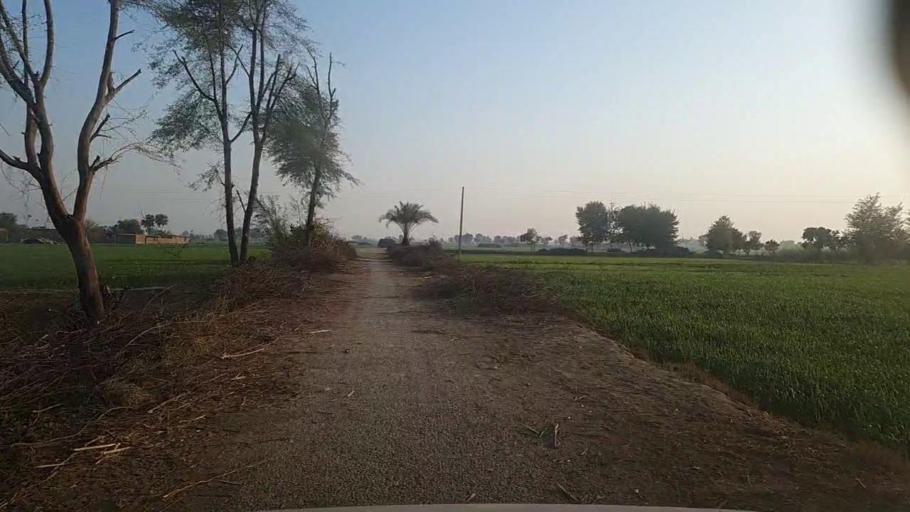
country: PK
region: Sindh
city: Khairpur
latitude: 28.0557
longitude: 69.7586
